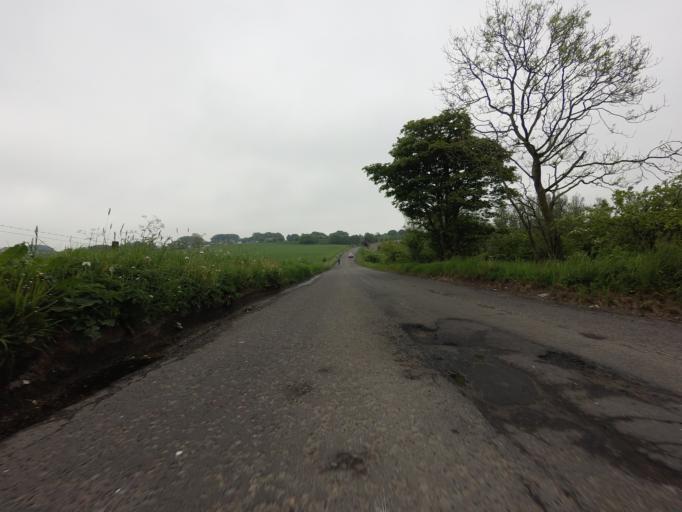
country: GB
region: Scotland
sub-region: Fife
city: Townhill
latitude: 56.1022
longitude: -3.4510
